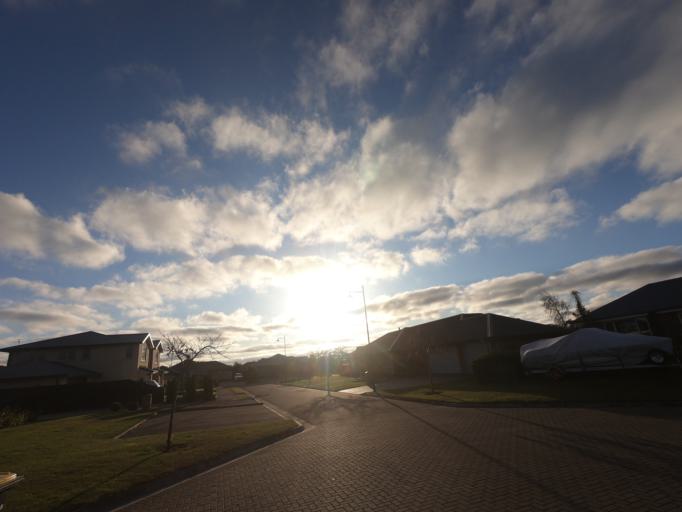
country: NZ
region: Canterbury
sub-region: Selwyn District
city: Prebbleton
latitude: -43.5688
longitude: 172.5668
